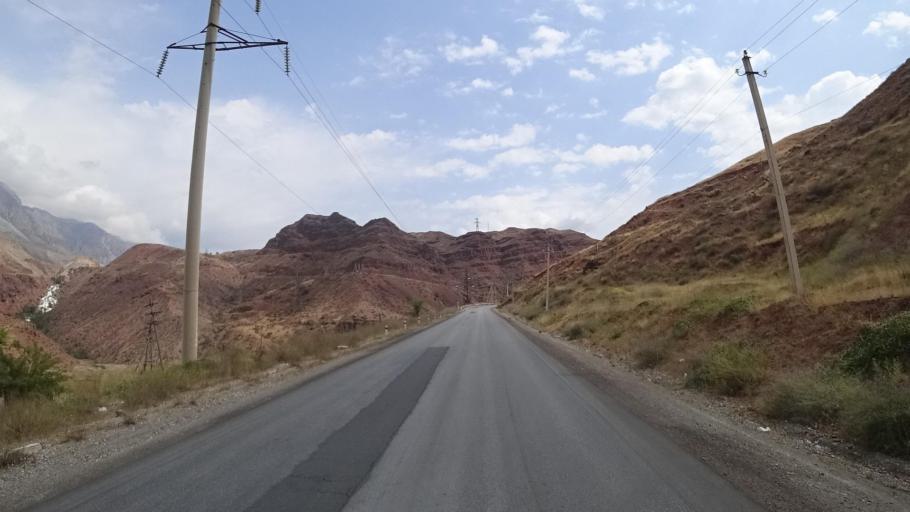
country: KG
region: Jalal-Abad
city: Toktogul
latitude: 41.6207
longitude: 72.6353
